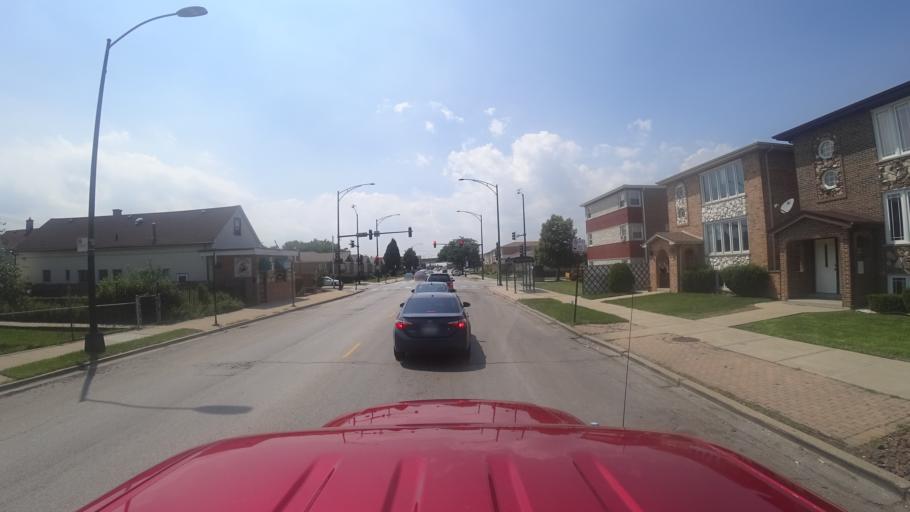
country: US
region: Illinois
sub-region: Cook County
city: Stickney
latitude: 41.7931
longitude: -87.7348
